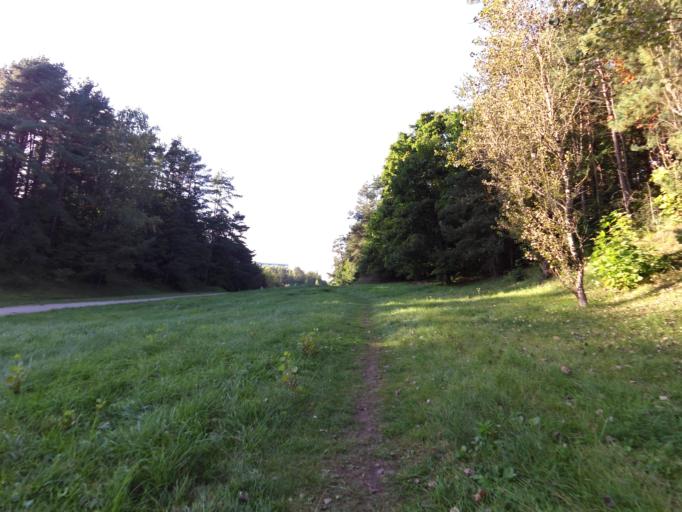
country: LT
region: Vilnius County
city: Seskine
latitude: 54.7012
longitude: 25.2366
